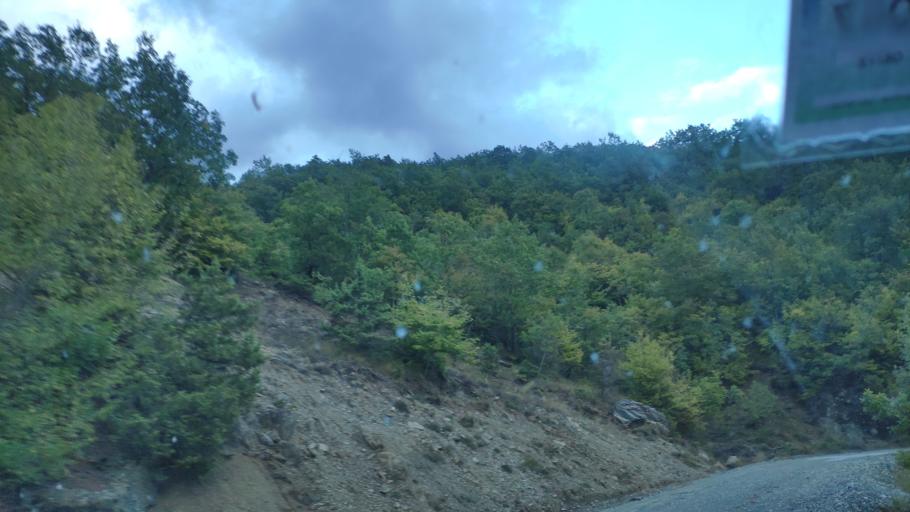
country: AL
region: Korce
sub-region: Rrethi i Kolonjes
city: Erseke
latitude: 40.2516
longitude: 20.8667
